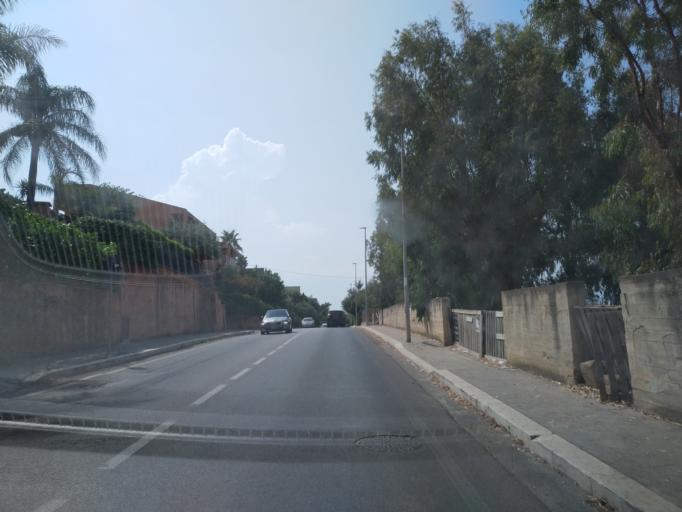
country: IT
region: Sicily
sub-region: Palermo
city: Cefalu
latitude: 38.0313
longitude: 14.0052
